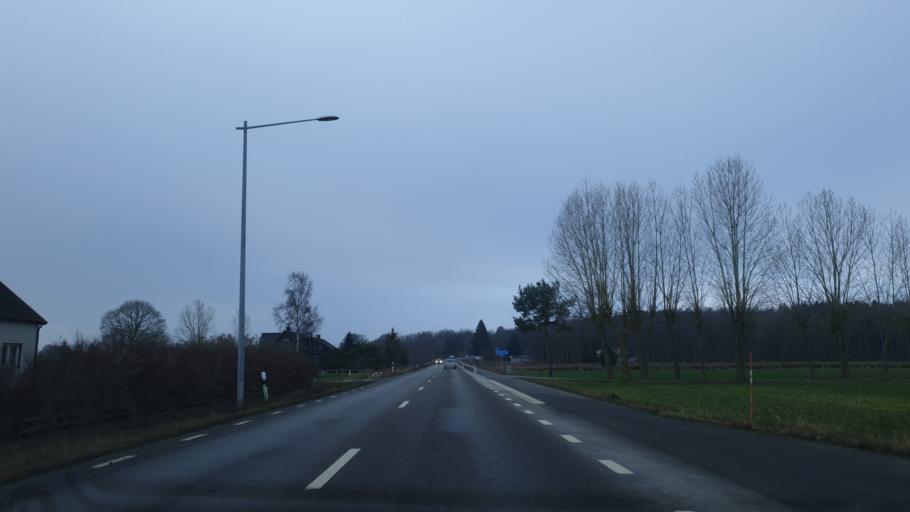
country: SE
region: Blekinge
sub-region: Solvesborgs Kommun
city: Soelvesborg
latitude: 56.0978
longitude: 14.6620
